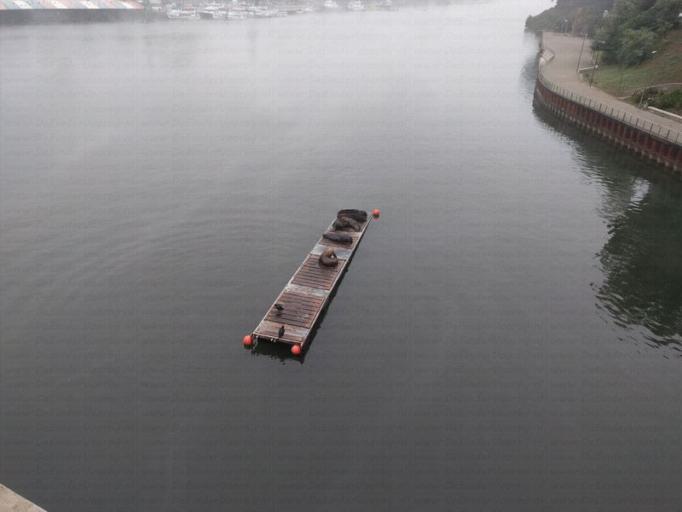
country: CL
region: Los Rios
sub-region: Provincia de Valdivia
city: Valdivia
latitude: -39.8114
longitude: -73.2500
